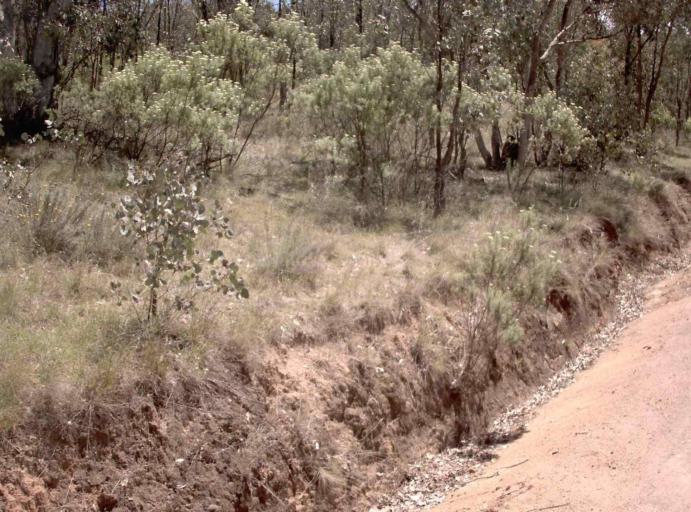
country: AU
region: New South Wales
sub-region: Snowy River
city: Jindabyne
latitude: -36.9365
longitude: 148.3496
